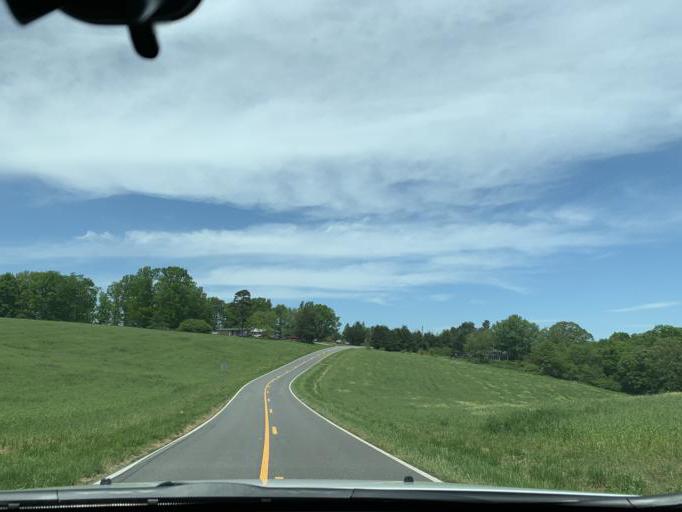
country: US
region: Georgia
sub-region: Hall County
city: Flowery Branch
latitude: 34.2816
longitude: -84.0221
